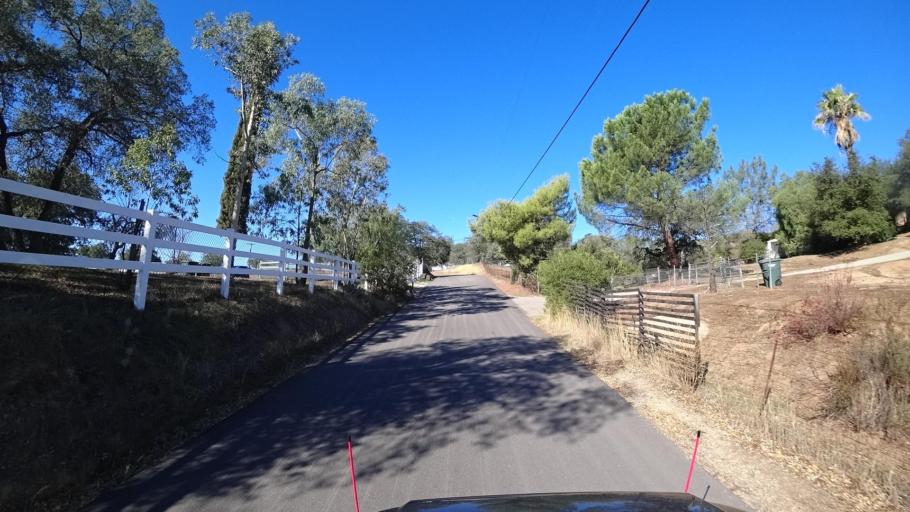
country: US
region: California
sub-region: San Diego County
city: Jamul
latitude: 32.6780
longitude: -116.7323
